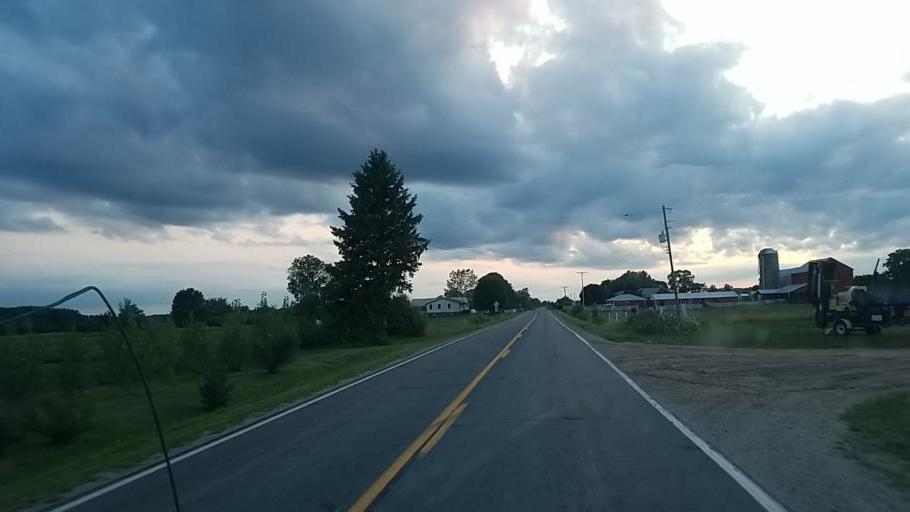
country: US
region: Michigan
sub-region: Newaygo County
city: Fremont
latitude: 43.4677
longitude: -86.0636
